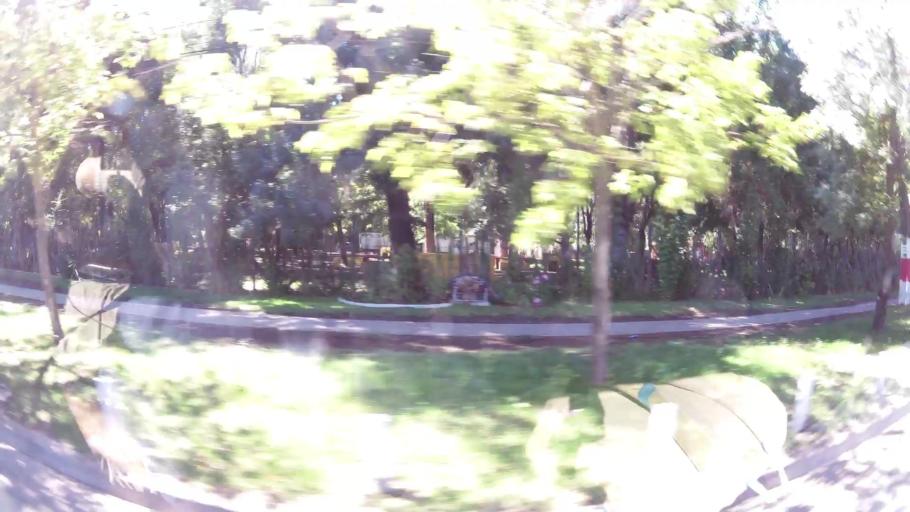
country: CL
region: Maule
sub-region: Provincia de Curico
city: Curico
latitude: -34.9763
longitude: -71.2322
